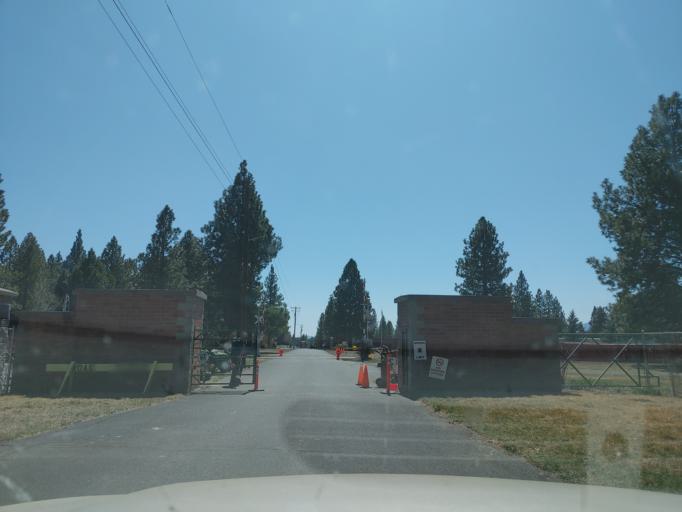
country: US
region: Oregon
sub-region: Klamath County
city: Klamath Falls
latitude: 42.5592
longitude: -121.8869
